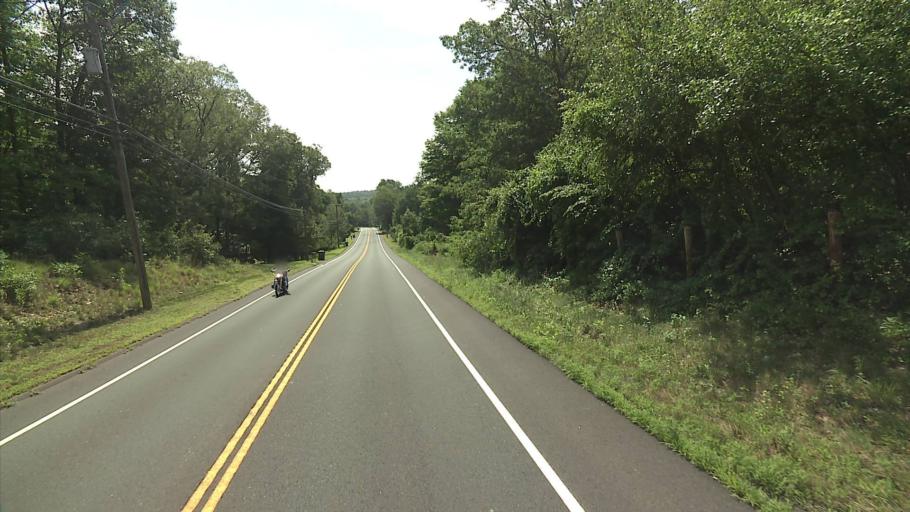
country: US
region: Connecticut
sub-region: Tolland County
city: Rockville
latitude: 41.8383
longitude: -72.4085
